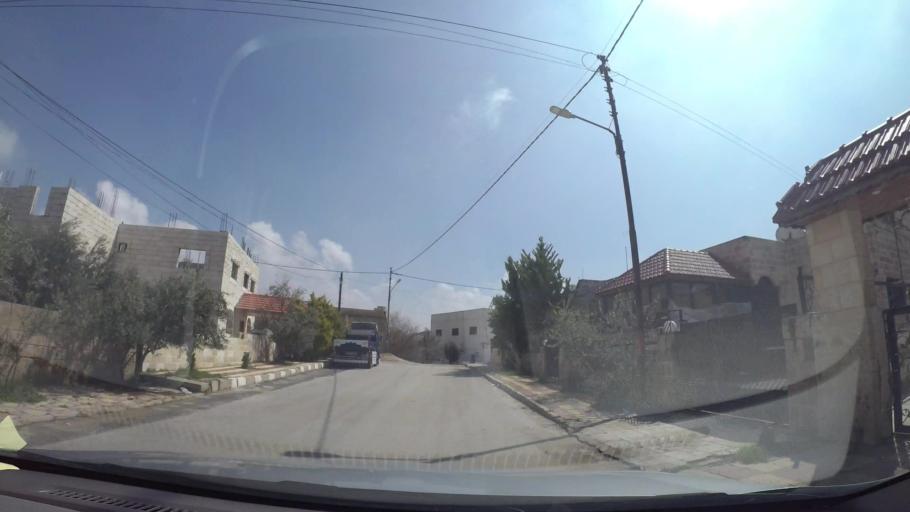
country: JO
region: Amman
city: Al Bunayyat ash Shamaliyah
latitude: 31.8917
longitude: 35.8943
